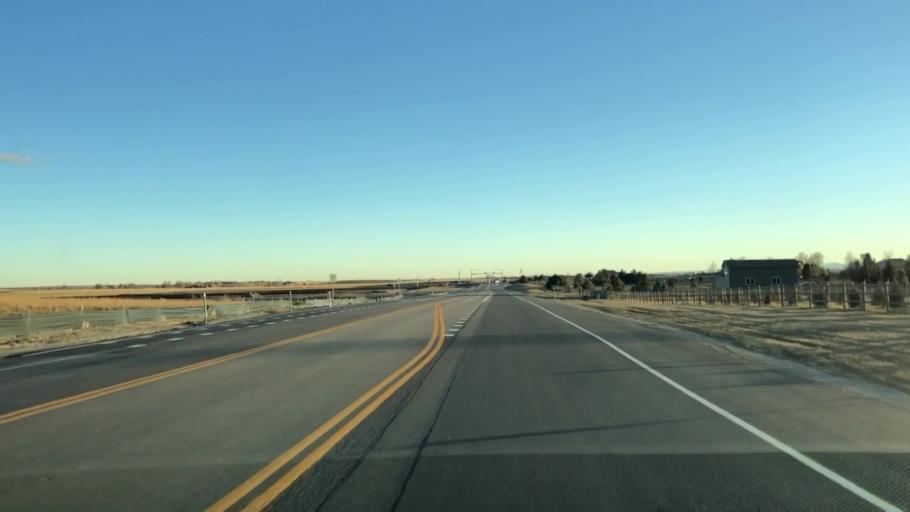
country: US
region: Colorado
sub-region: Weld County
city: Windsor
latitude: 40.4409
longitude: -104.9443
